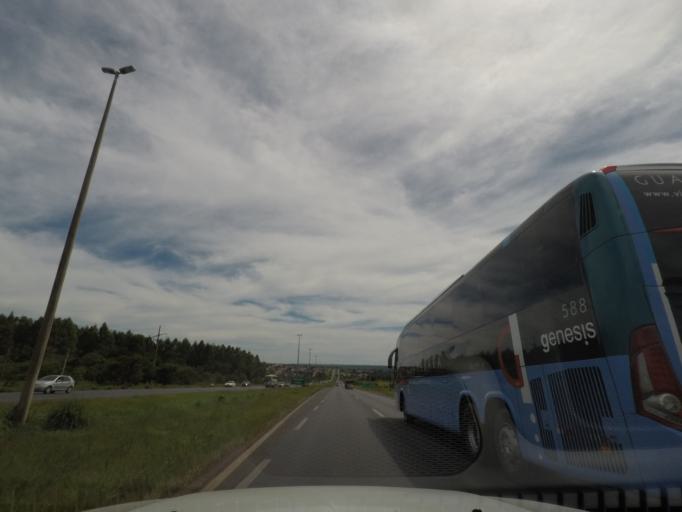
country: BR
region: Goias
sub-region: Planaltina
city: Planaltina
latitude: -15.6138
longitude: -47.7034
